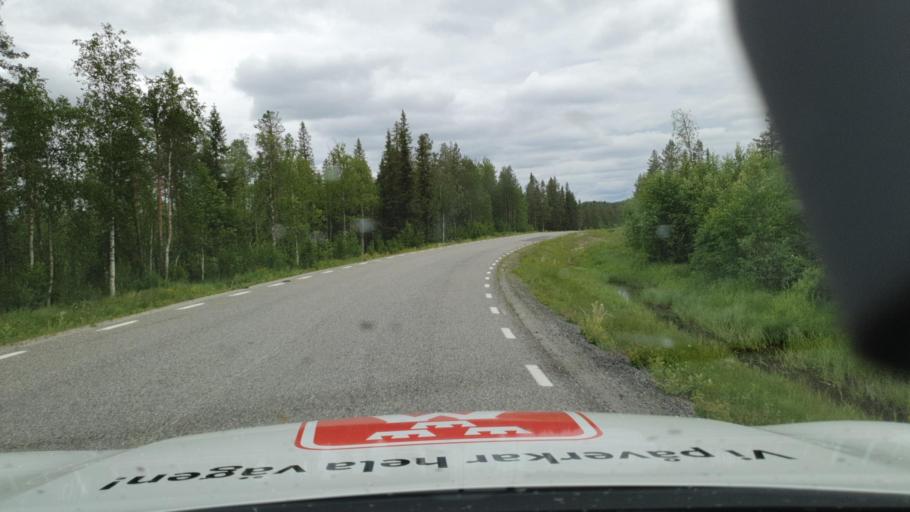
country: SE
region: Vaesterbotten
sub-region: Lycksele Kommun
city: Soderfors
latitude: 64.2724
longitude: 18.2034
